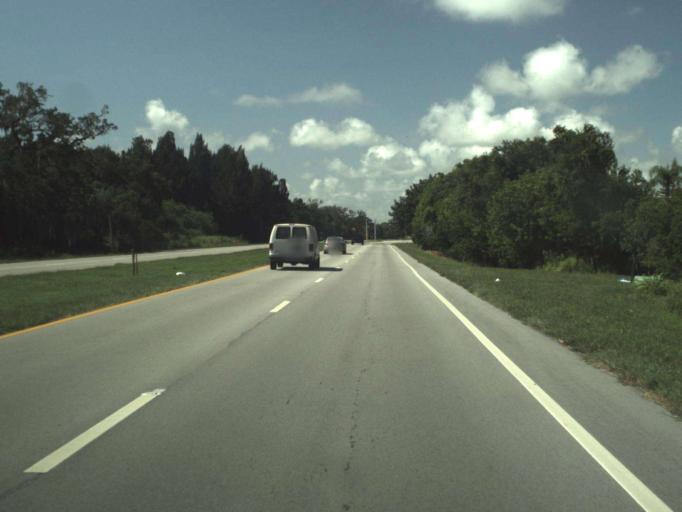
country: US
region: Florida
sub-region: Indian River County
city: Vero Beach
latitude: 27.6200
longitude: -80.3810
